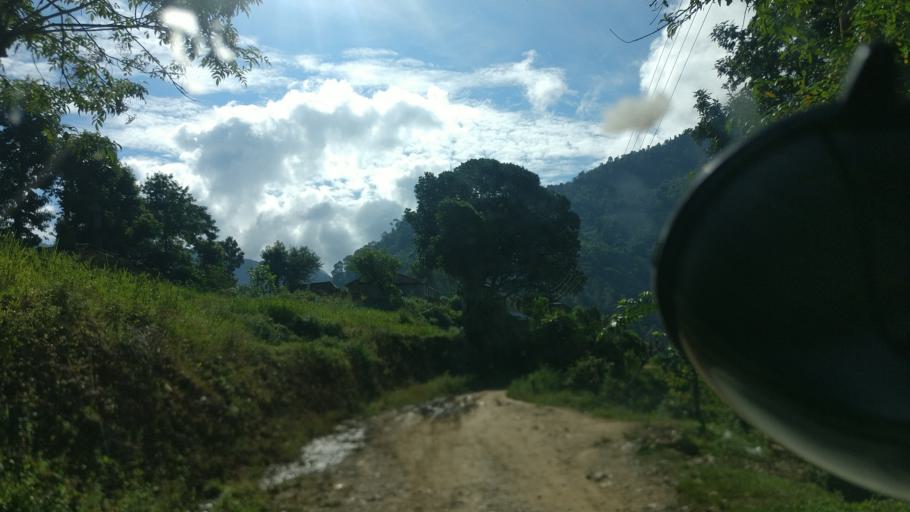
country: NP
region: Western Region
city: Baglung
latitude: 28.1347
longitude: 83.6567
